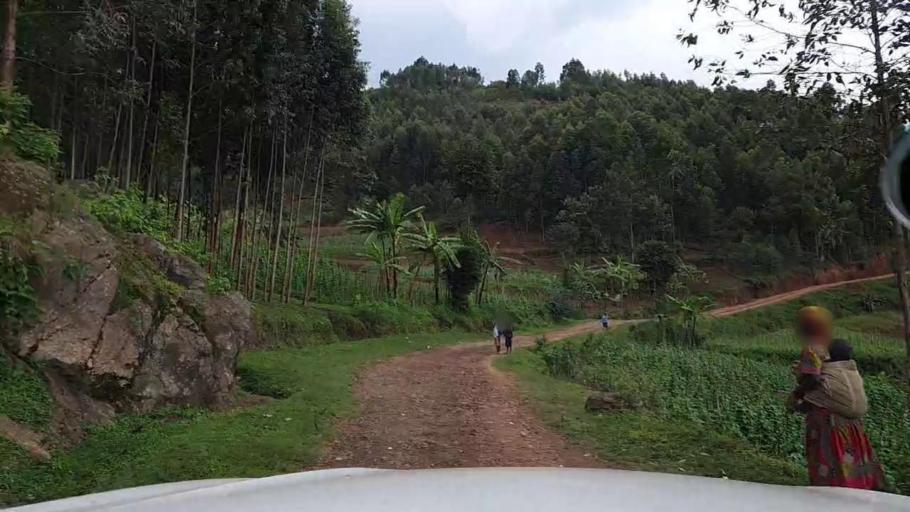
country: RW
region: Northern Province
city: Byumba
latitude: -1.6258
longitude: 29.9212
